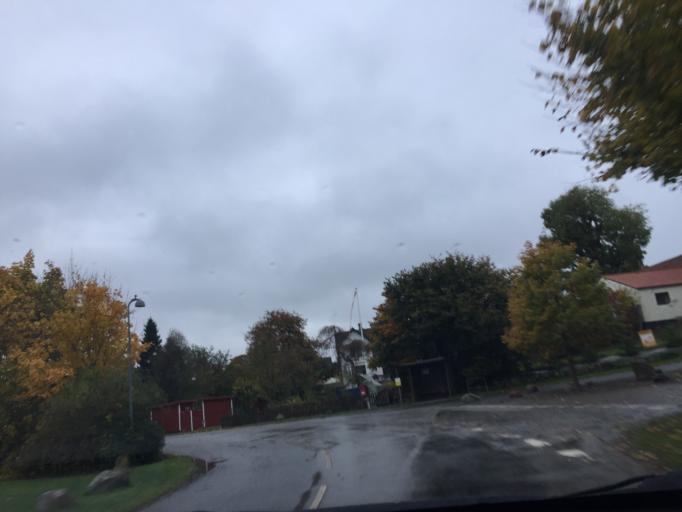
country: DK
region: Zealand
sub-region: Ringsted Kommune
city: Ringsted
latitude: 55.4906
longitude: 11.7687
